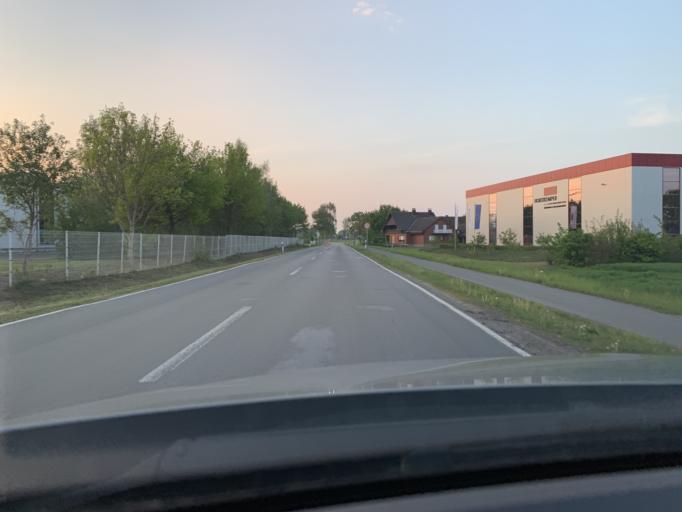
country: DE
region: North Rhine-Westphalia
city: Rietberg
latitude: 51.7669
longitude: 8.3854
